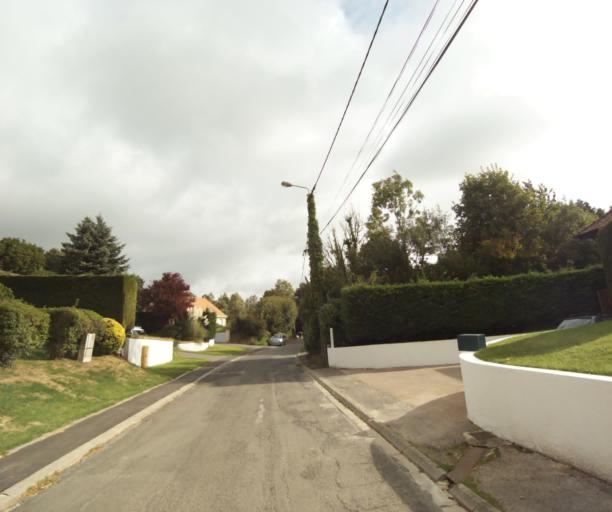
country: FR
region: Nord-Pas-de-Calais
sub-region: Departement du Pas-de-Calais
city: Etaples
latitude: 50.5275
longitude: 1.6810
